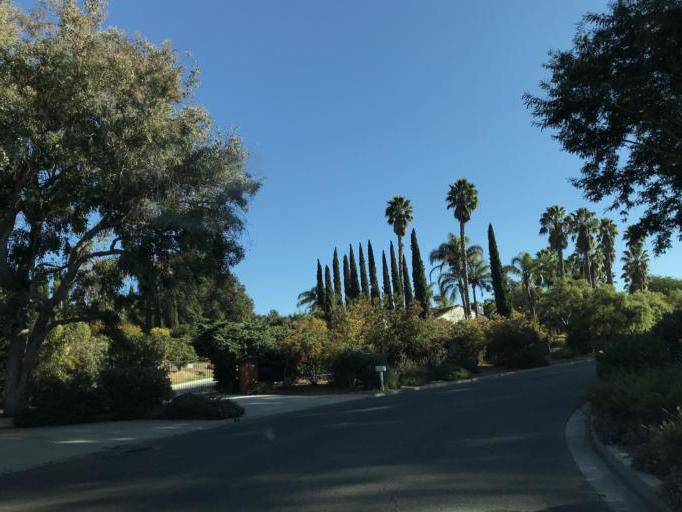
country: US
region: California
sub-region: Santa Barbara County
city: Goleta
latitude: 34.4544
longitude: -119.8061
